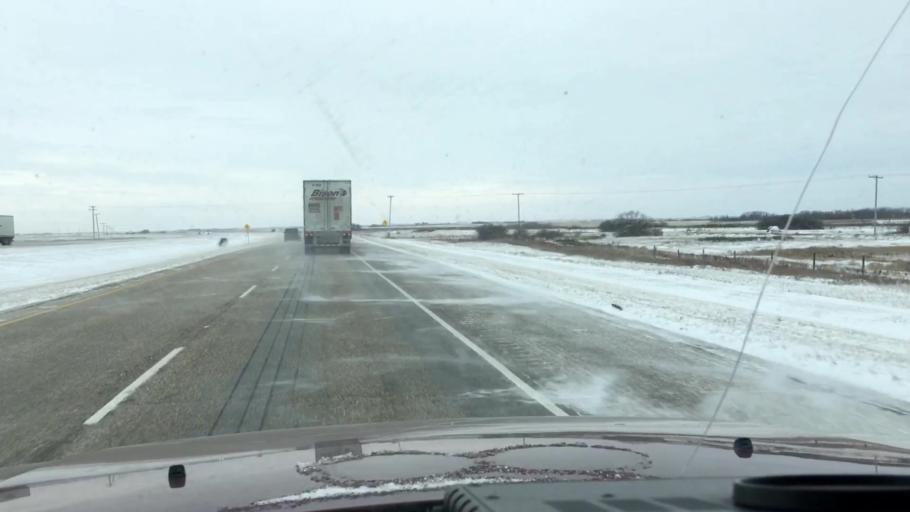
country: CA
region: Saskatchewan
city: Saskatoon
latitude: 51.6122
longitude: -106.4125
